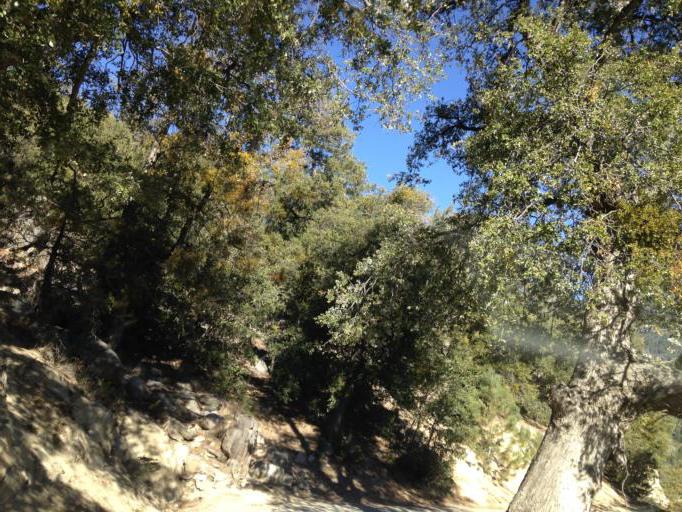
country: US
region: California
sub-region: Riverside County
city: Idyllwild-Pine Cove
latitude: 33.8122
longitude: -116.7495
